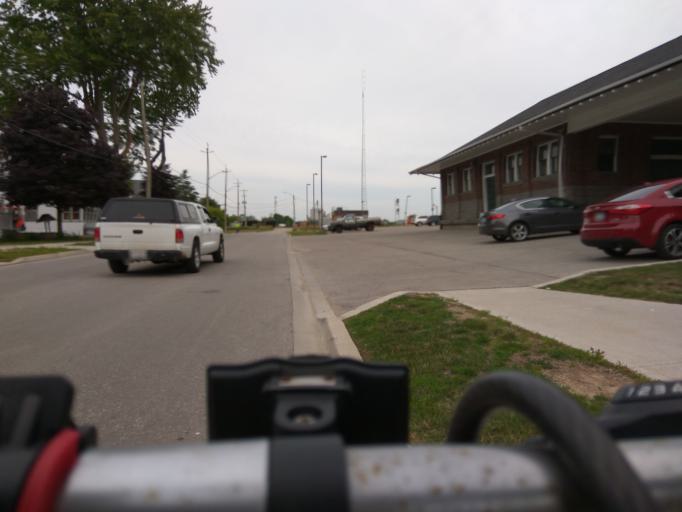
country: CA
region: Ontario
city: Stratford
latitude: 43.3647
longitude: -80.9755
